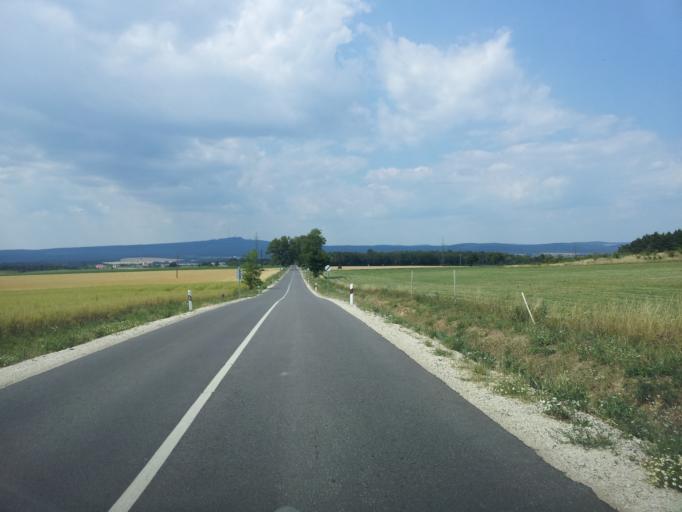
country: HU
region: Veszprem
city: Zanka
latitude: 46.9577
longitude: 17.7015
